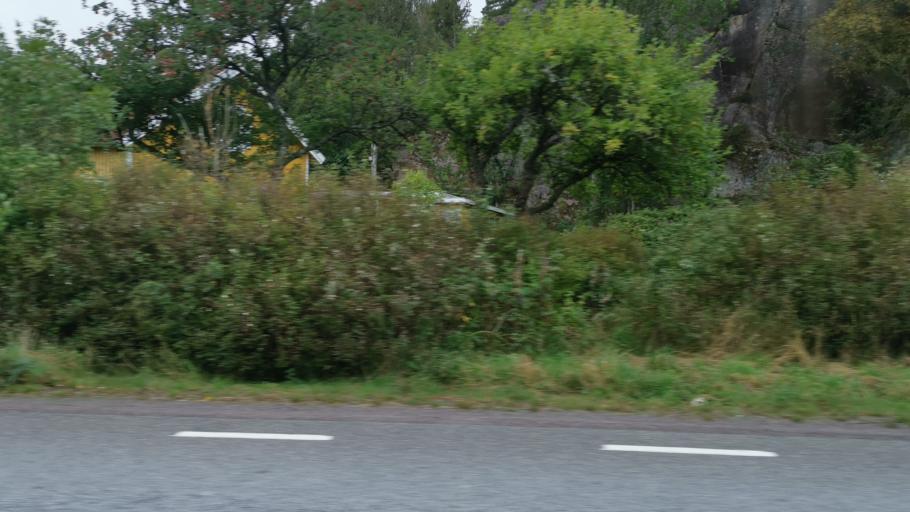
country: SE
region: Vaestra Goetaland
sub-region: Lysekils Kommun
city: Brastad
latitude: 58.5622
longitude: 11.4725
